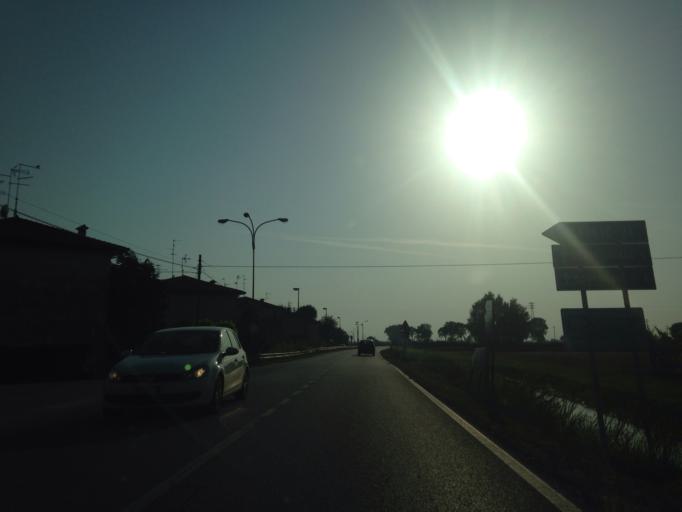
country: IT
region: Veneto
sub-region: Provincia di Venezia
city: Fossalta di Portogruaro
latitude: 45.7557
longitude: 12.9035
